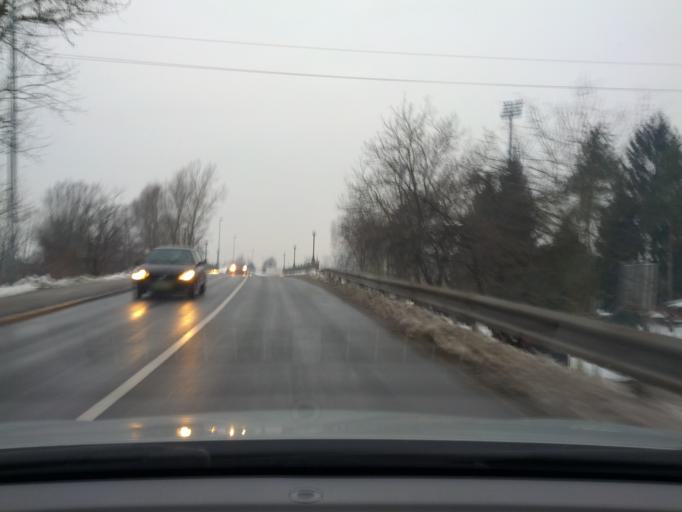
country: SI
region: Domzale
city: Domzale
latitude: 46.1358
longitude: 14.6040
